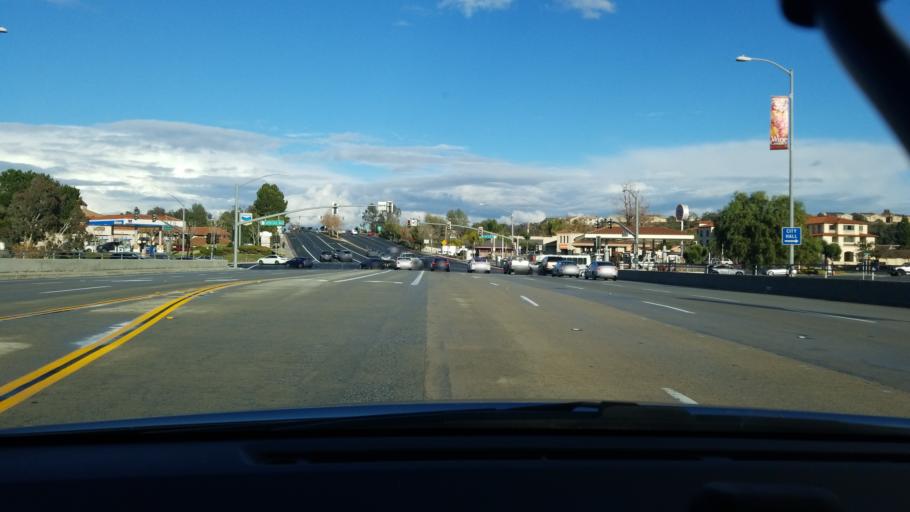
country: US
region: California
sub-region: Riverside County
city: Temecula
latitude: 33.4987
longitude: -117.1548
